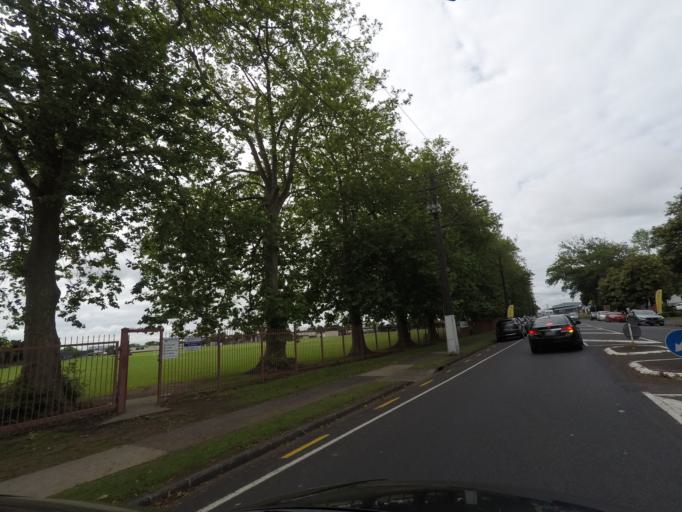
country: NZ
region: Auckland
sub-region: Auckland
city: Rosebank
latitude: -36.8661
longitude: 174.6158
